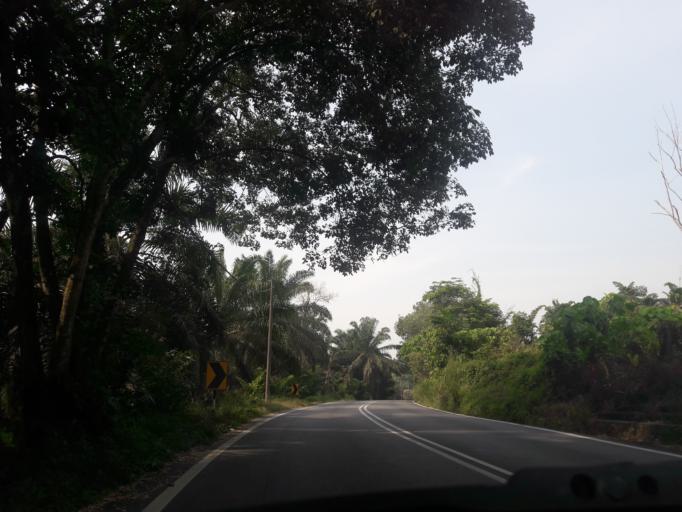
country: MY
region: Kedah
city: Kulim
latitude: 5.3584
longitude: 100.5210
